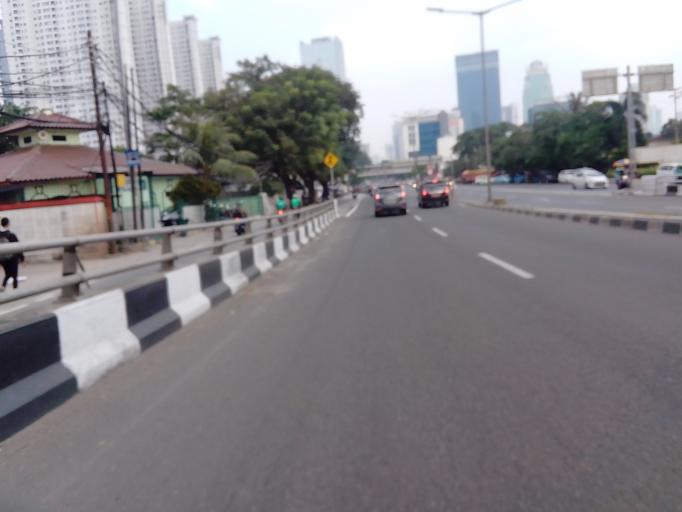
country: ID
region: Jakarta Raya
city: Jakarta
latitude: -6.2029
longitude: 106.8161
